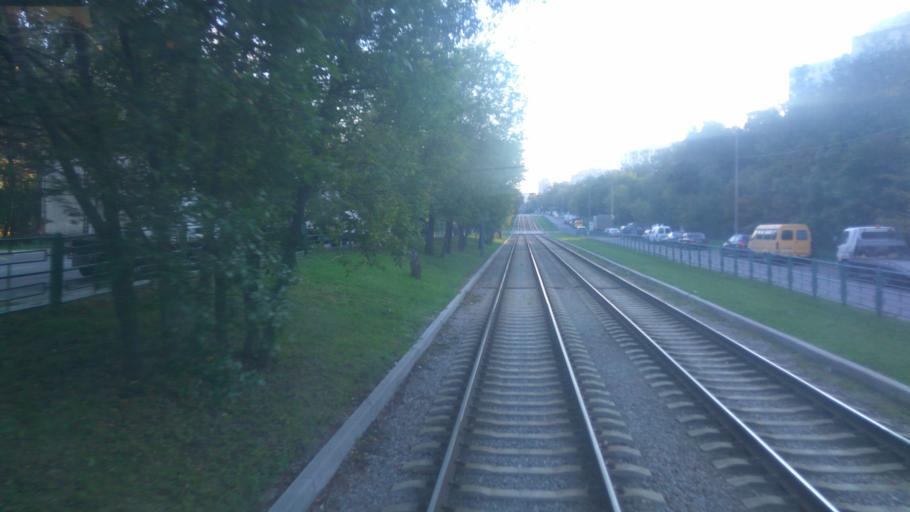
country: RU
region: Moscow
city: Metrogorodok
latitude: 55.8267
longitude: 37.7628
